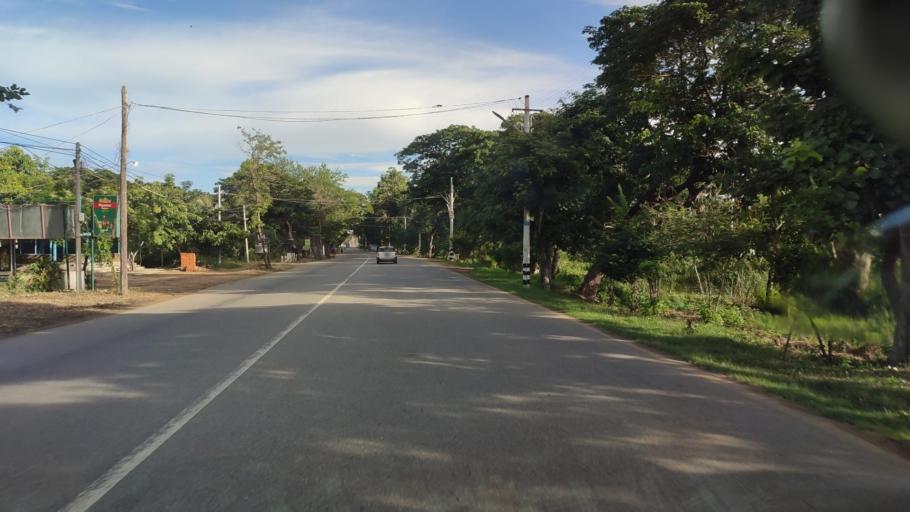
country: MM
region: Mandalay
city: Yamethin
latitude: 20.1453
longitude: 96.1942
